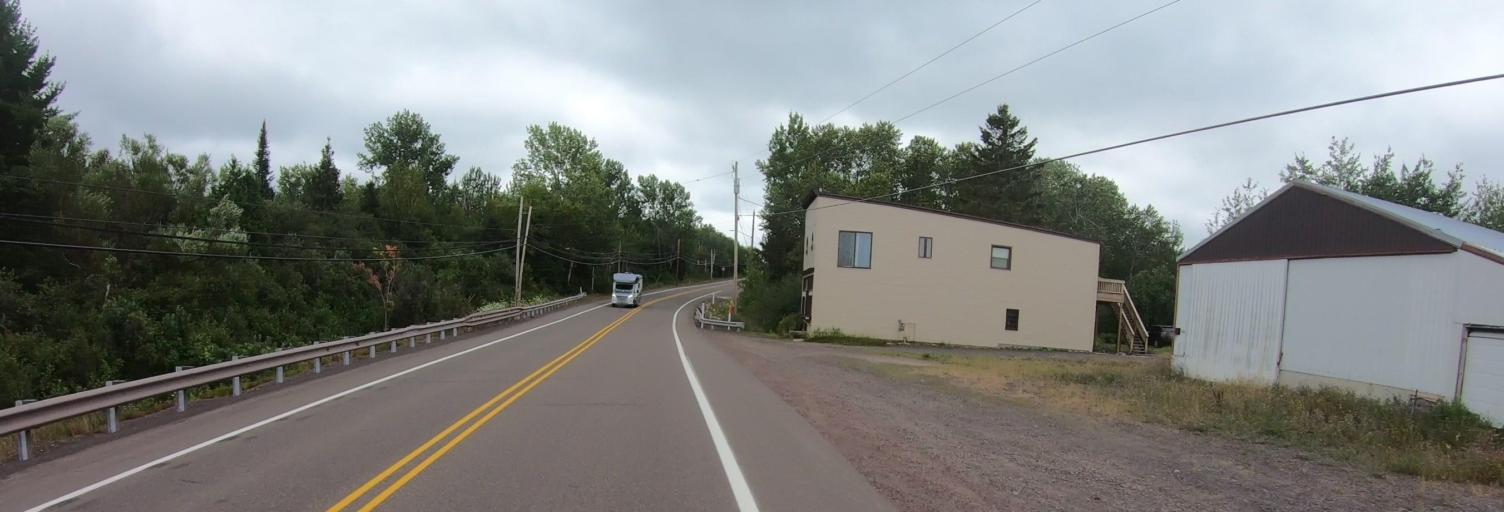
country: US
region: Michigan
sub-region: Houghton County
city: Laurium
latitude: 47.2816
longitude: -88.4112
